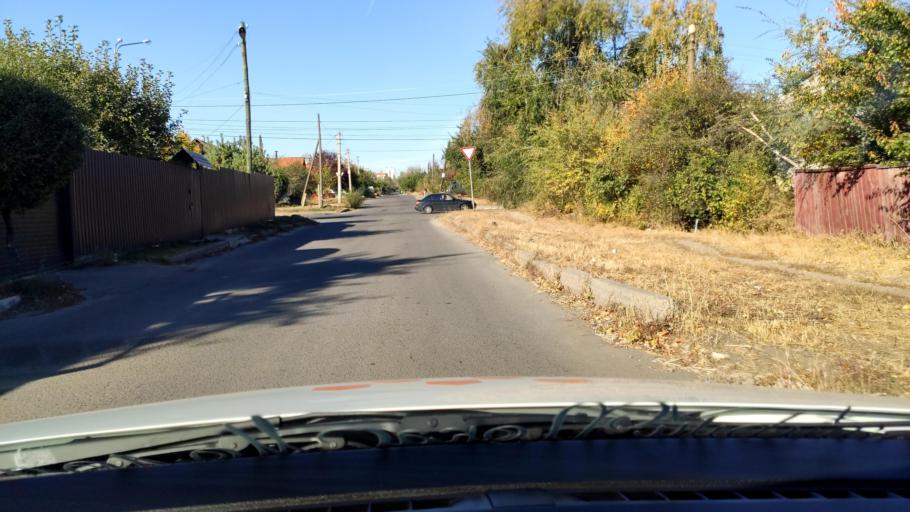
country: RU
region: Voronezj
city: Voronezh
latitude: 51.6941
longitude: 39.1693
